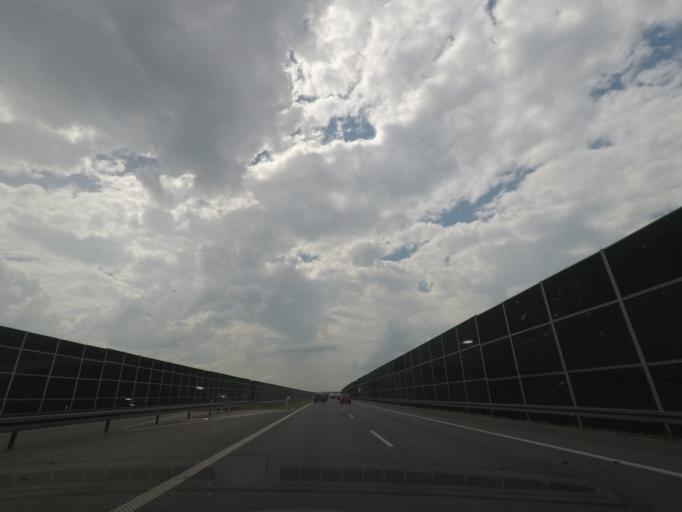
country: PL
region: Masovian Voivodeship
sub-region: Powiat pruszkowski
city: Brwinow
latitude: 52.1692
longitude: 20.7471
